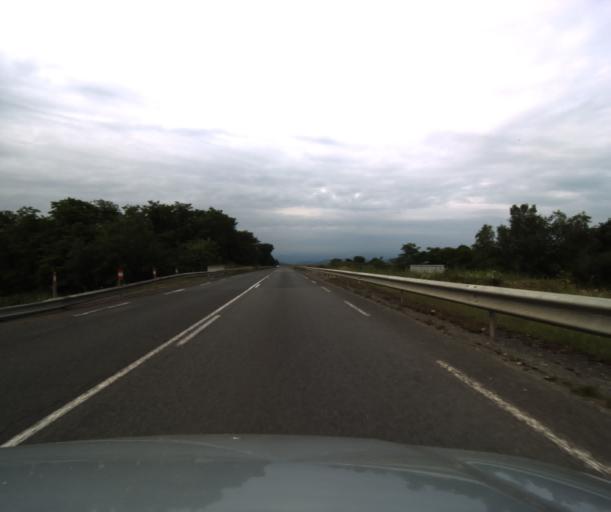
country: FR
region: Midi-Pyrenees
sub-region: Departement des Hautes-Pyrenees
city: Juillan
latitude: 43.2173
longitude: 0.0158
